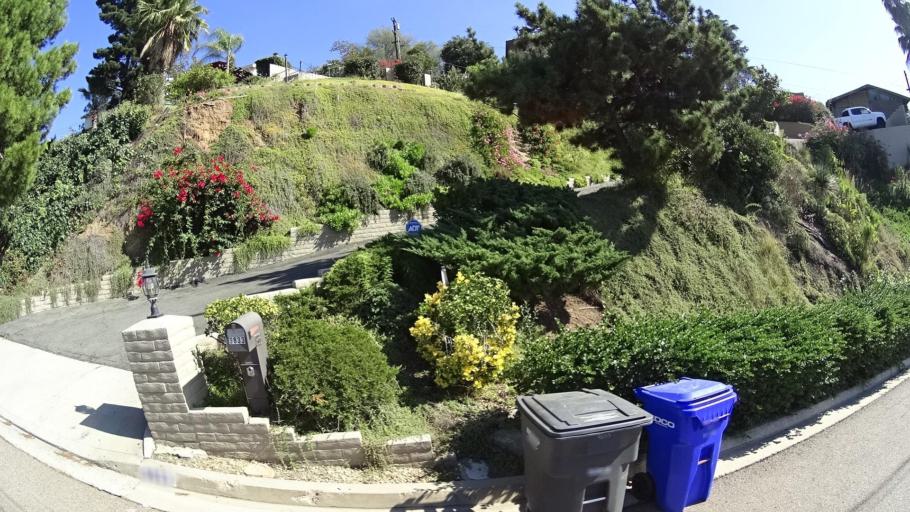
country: US
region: California
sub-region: San Diego County
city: Casa de Oro-Mount Helix
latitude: 32.7598
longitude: -116.9817
